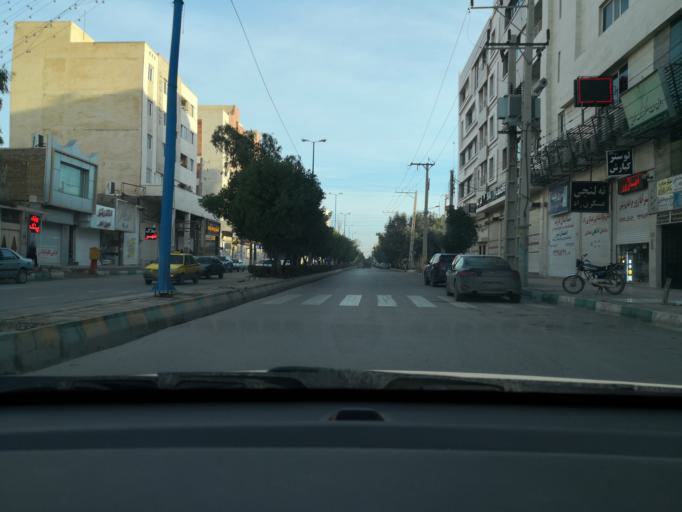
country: IR
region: Khuzestan
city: Ahvaz
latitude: 31.3503
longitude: 48.6767
